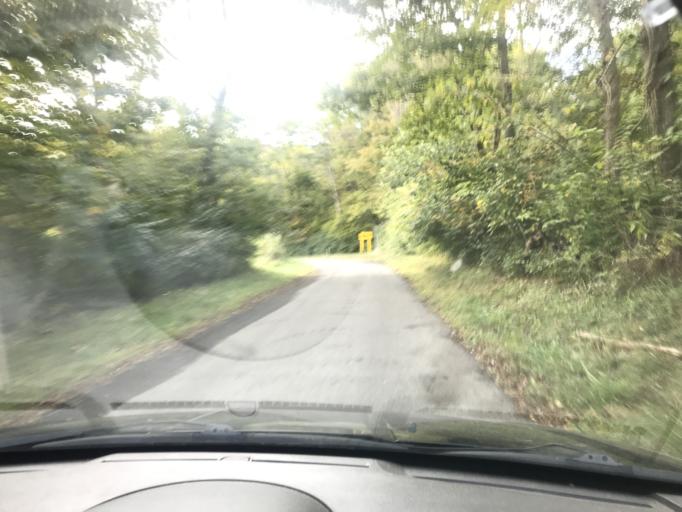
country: US
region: Ohio
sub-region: Logan County
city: West Liberty
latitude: 40.2263
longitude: -83.6662
